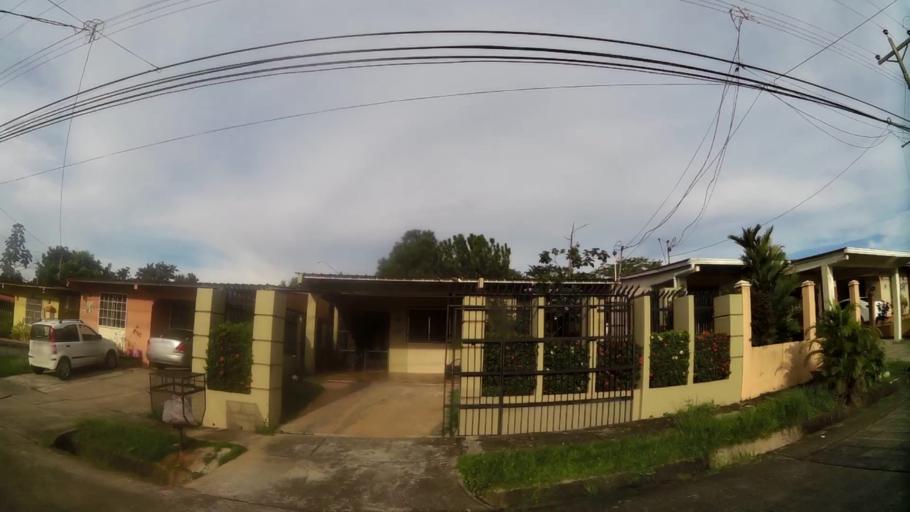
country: PA
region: Panama
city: La Chorrera
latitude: 8.8966
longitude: -79.7679
